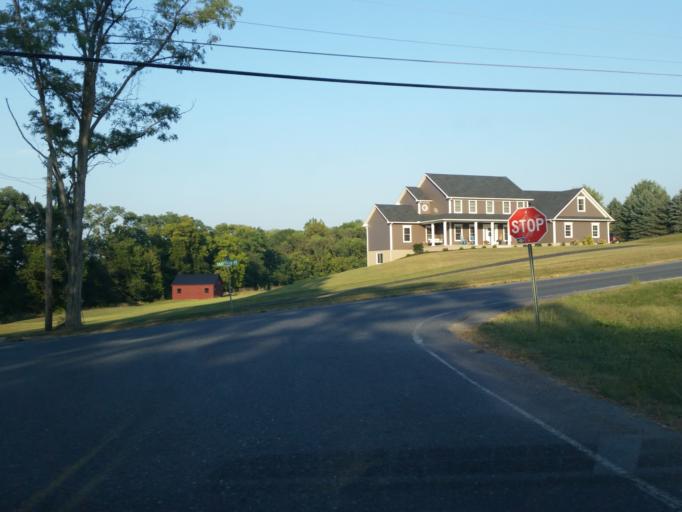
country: US
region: Pennsylvania
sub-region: Lebanon County
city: Annville
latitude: 40.3414
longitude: -76.5273
